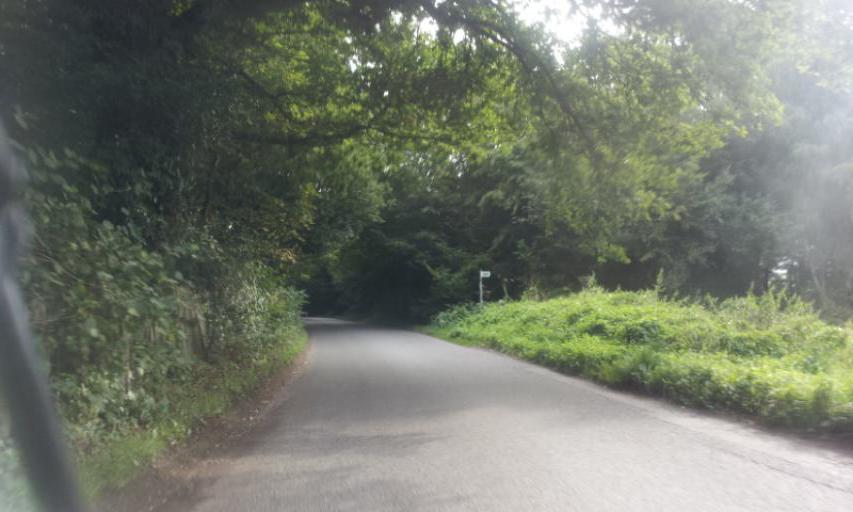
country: GB
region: England
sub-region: Kent
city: Hadlow
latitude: 51.2358
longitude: 0.2995
